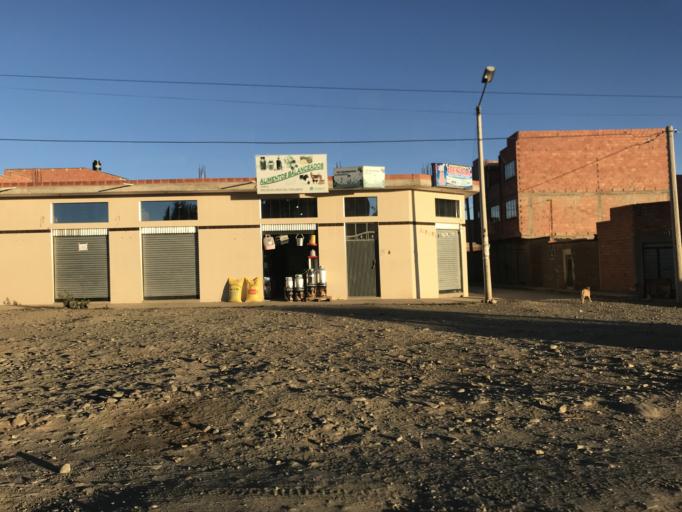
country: BO
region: La Paz
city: La Paz
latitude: -16.4990
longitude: -68.2325
